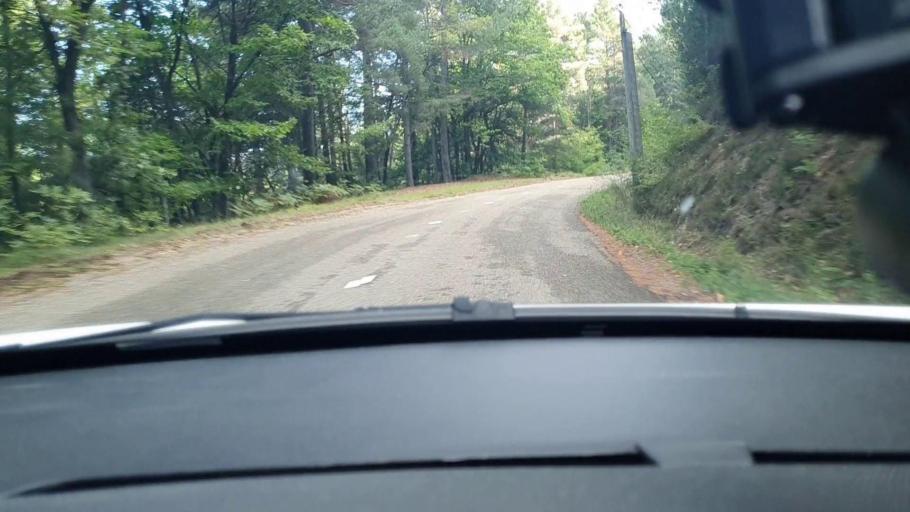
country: FR
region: Rhone-Alpes
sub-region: Departement de l'Ardeche
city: Les Vans
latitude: 44.3986
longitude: 3.9988
